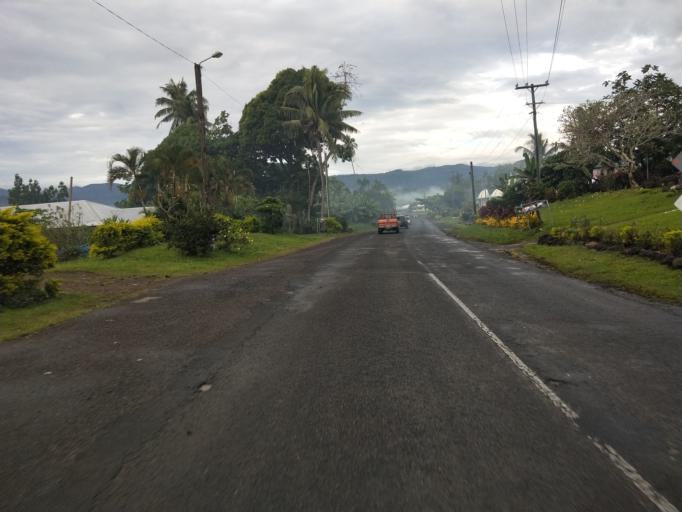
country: WS
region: Tuamasaga
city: Vaiusu
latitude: -13.8121
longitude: -171.8092
